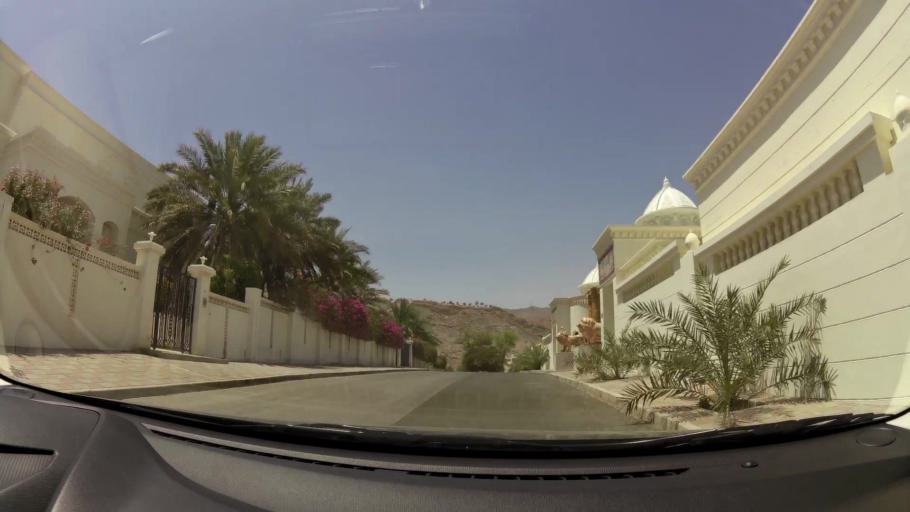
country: OM
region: Muhafazat Masqat
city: Bawshar
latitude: 23.5978
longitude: 58.4752
